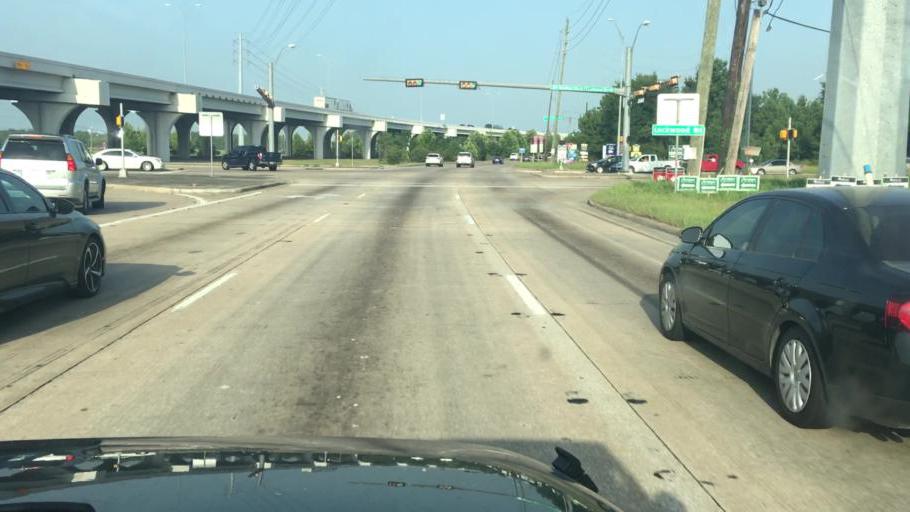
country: US
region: Texas
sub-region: Harris County
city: Atascocita
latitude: 29.9339
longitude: -95.2122
